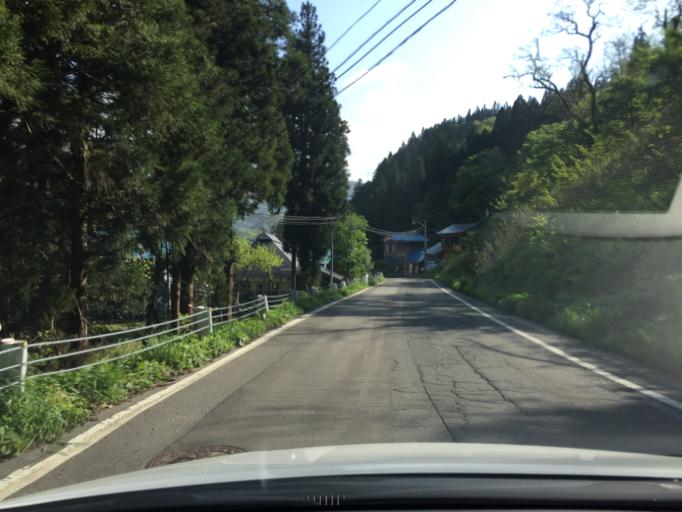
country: JP
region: Fukushima
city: Kitakata
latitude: 37.6781
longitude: 139.5739
